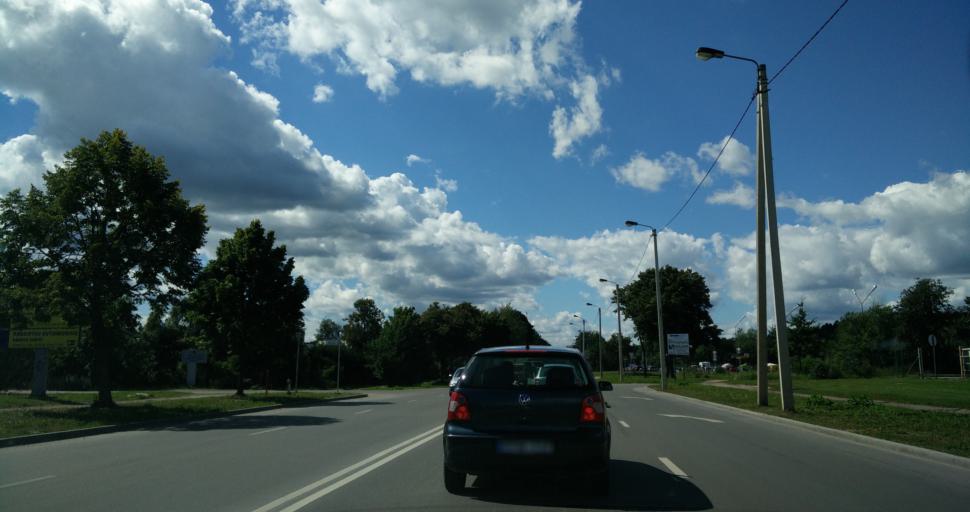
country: LT
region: Kauno apskritis
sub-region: Kauno rajonas
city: Akademija (Kaunas)
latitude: 54.9204
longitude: 23.8246
